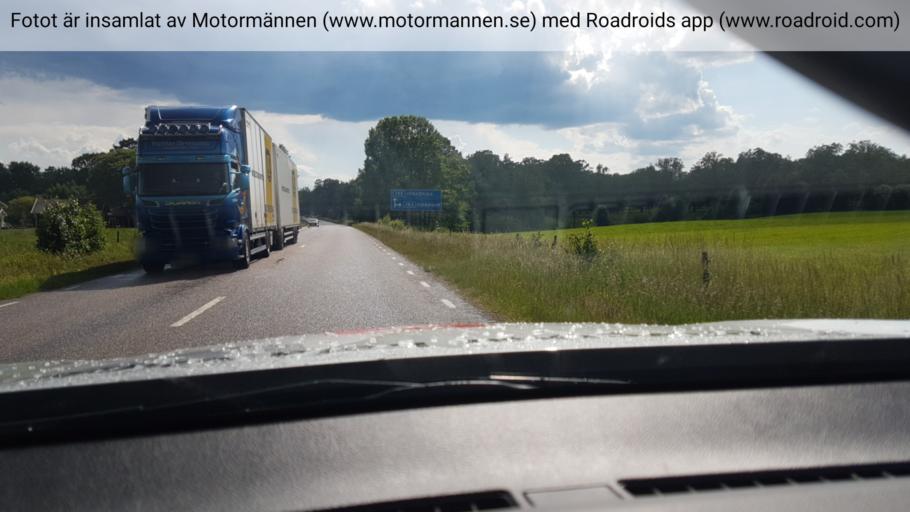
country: SE
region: Vaestra Goetaland
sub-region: Hjo Kommun
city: Hjo
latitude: 58.2289
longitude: 14.2140
